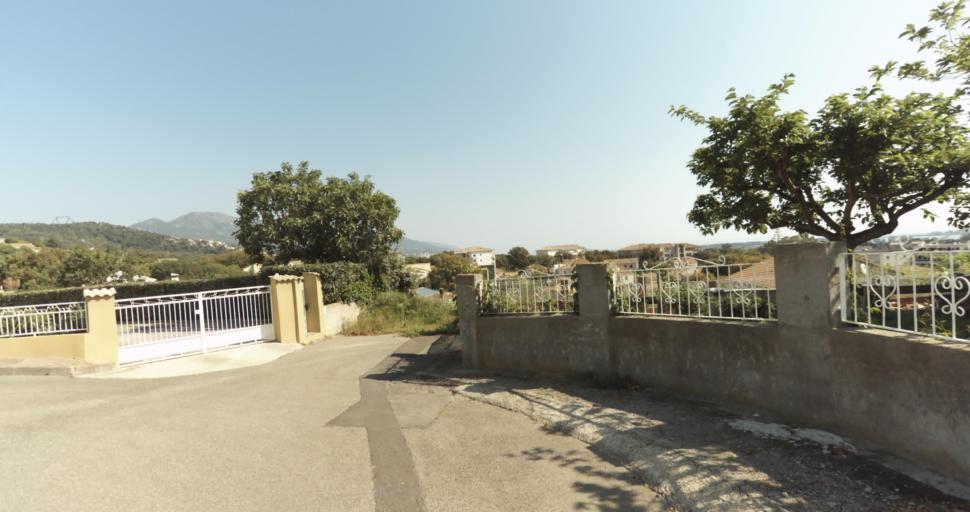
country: FR
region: Corsica
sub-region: Departement de la Haute-Corse
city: Biguglia
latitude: 42.6265
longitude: 9.4274
